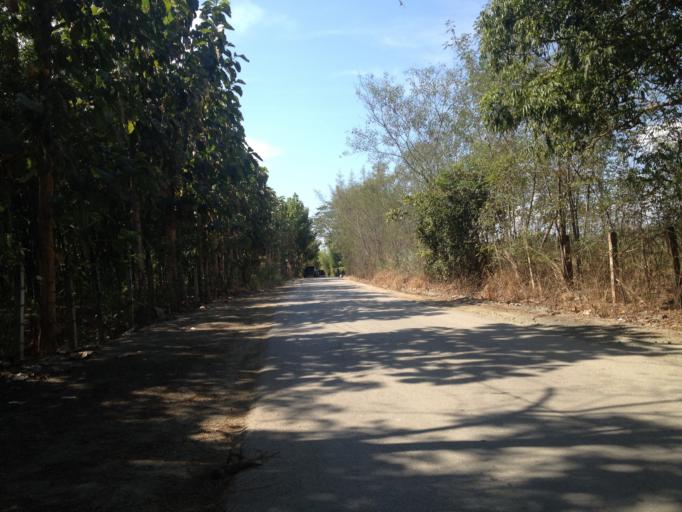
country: TH
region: Chiang Mai
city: Hang Dong
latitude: 18.6978
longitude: 98.8943
